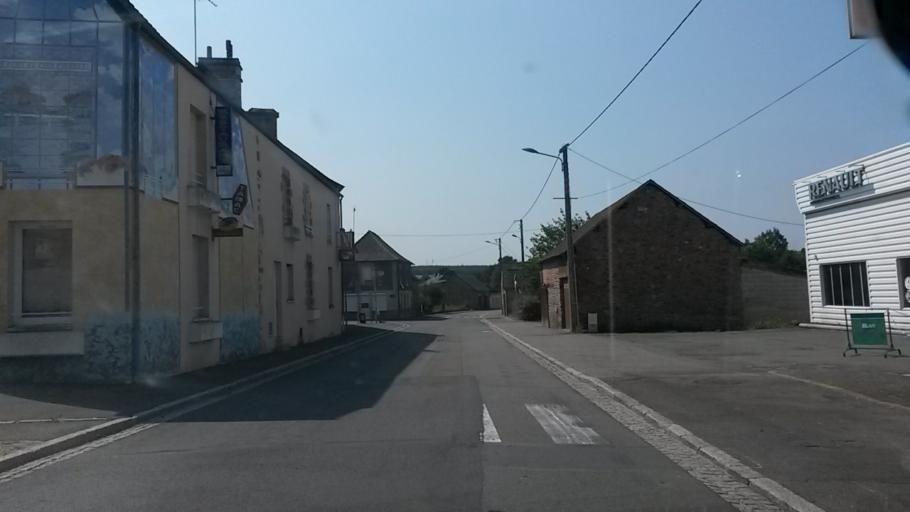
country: FR
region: Pays de la Loire
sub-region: Departement de la Mayenne
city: Saint-Pierre-des-Nids
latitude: 48.3697
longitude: -0.1468
